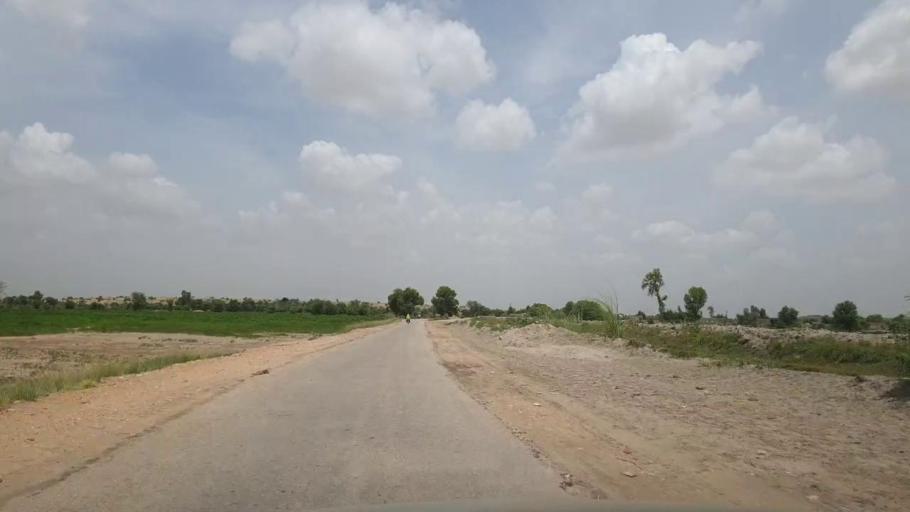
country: PK
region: Sindh
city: Kot Diji
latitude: 27.2007
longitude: 69.0543
